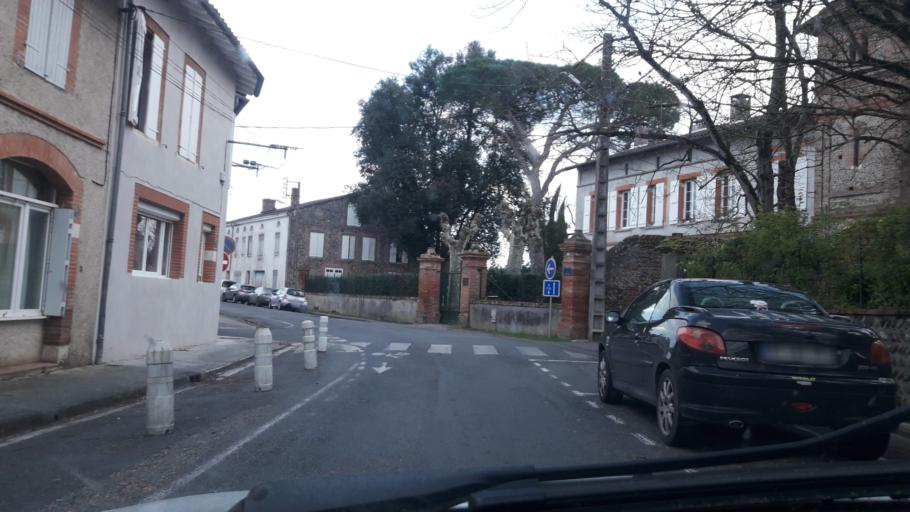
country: FR
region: Midi-Pyrenees
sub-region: Departement de la Haute-Garonne
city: Carbonne
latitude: 43.2960
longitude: 1.2213
